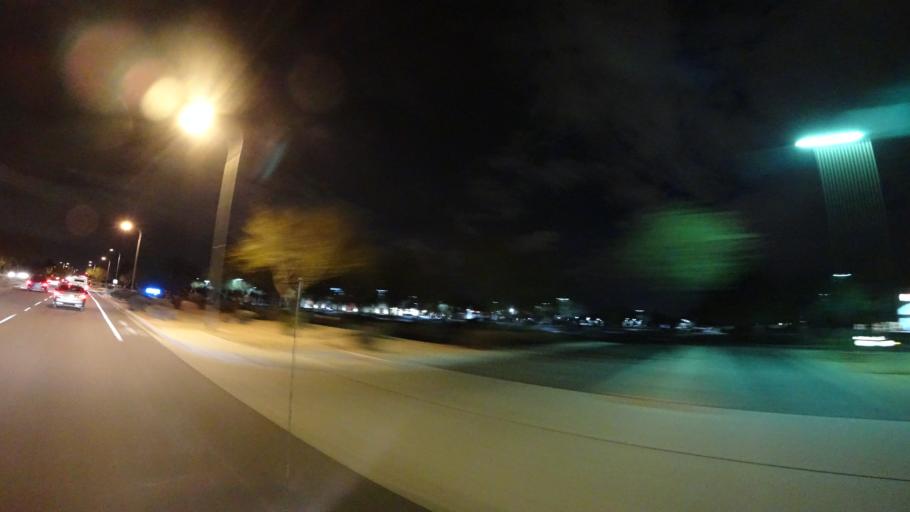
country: US
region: Arizona
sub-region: Maricopa County
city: Chandler
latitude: 33.2783
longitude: -111.8586
